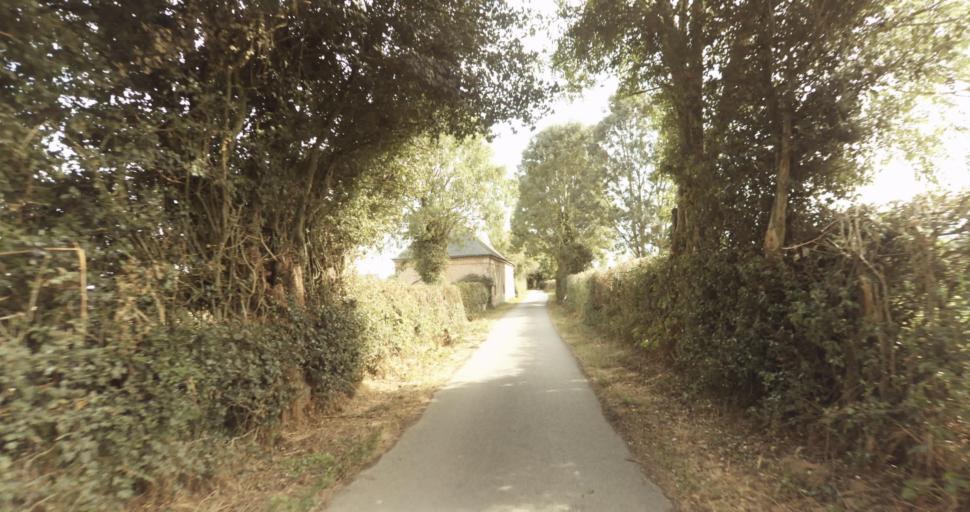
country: FR
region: Lower Normandy
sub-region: Departement de l'Orne
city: Gace
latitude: 48.8583
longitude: 0.2565
